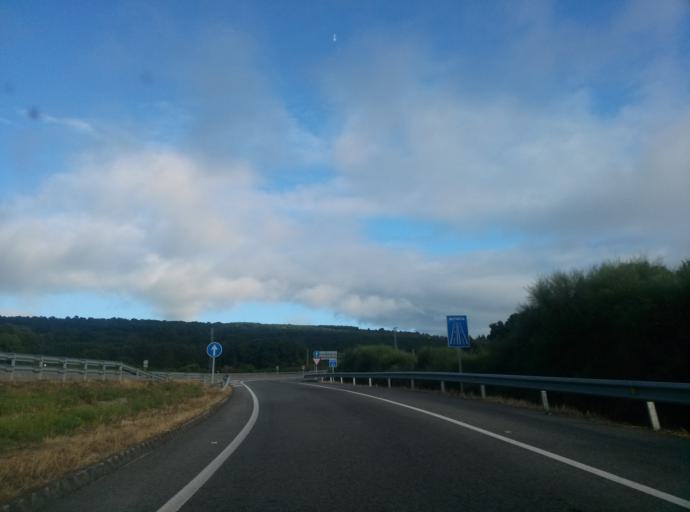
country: ES
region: Galicia
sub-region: Provincia da Coruna
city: As Pontes de Garcia Rodriguez
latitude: 43.3987
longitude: -7.7823
